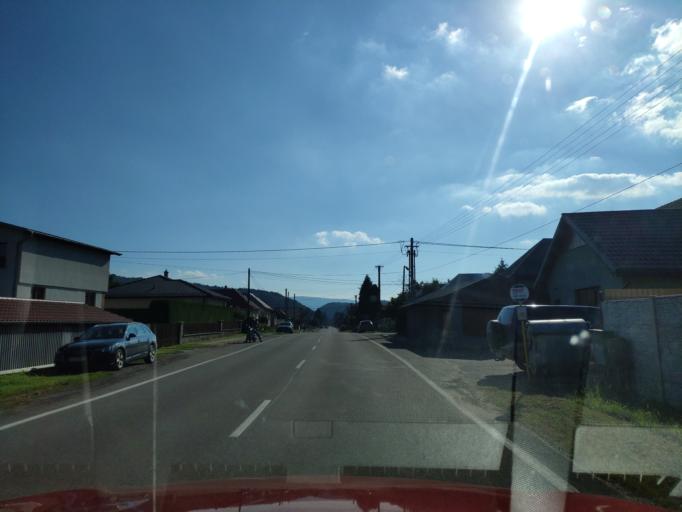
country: SK
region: Presovsky
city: Snina
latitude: 49.0073
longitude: 22.2391
